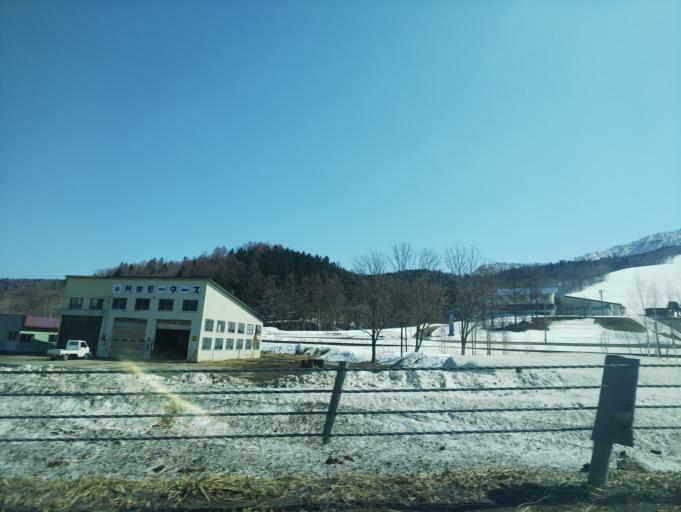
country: JP
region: Hokkaido
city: Nayoro
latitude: 44.7225
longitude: 142.2694
